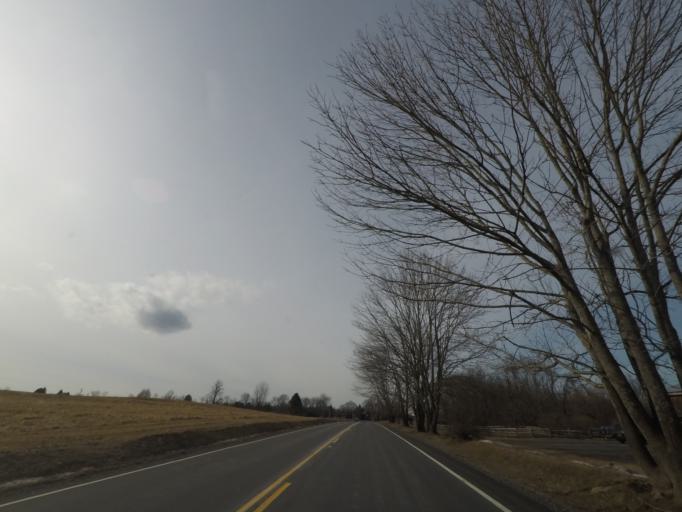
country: US
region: New York
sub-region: Columbia County
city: Valatie
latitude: 42.3958
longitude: -73.6477
